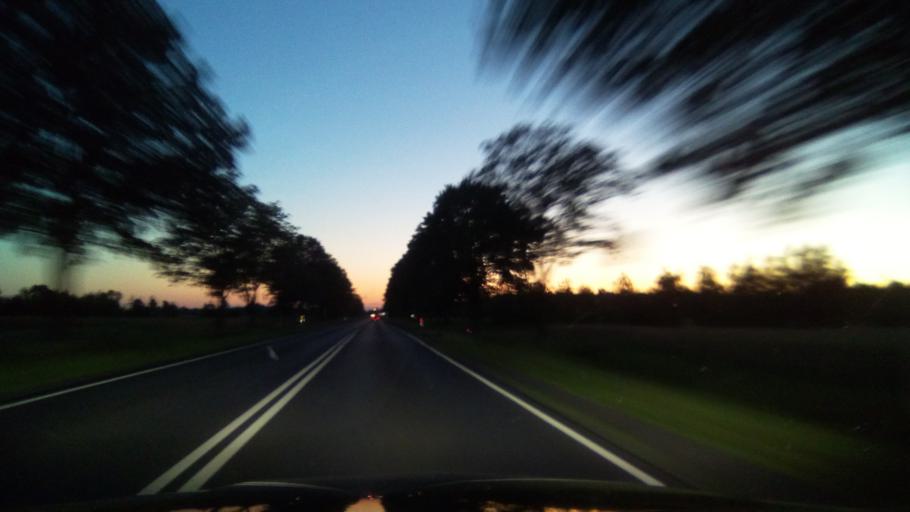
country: PL
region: Greater Poland Voivodeship
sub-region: Powiat koninski
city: Golina
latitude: 52.2475
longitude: 18.0300
